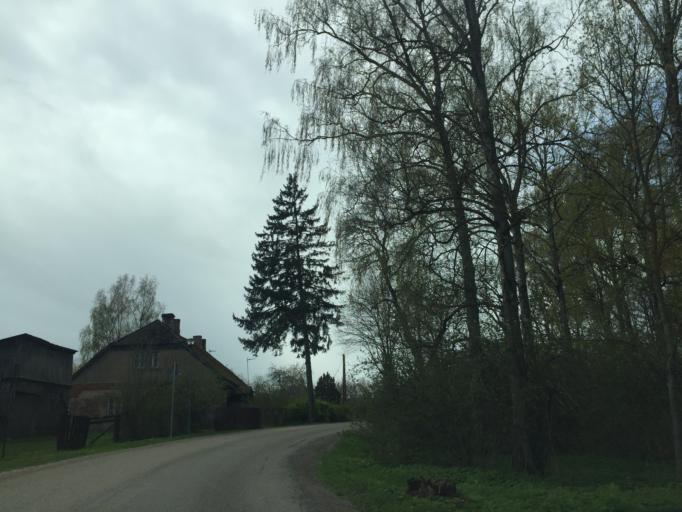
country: LV
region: Lecava
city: Iecava
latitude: 56.5918
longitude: 24.1961
